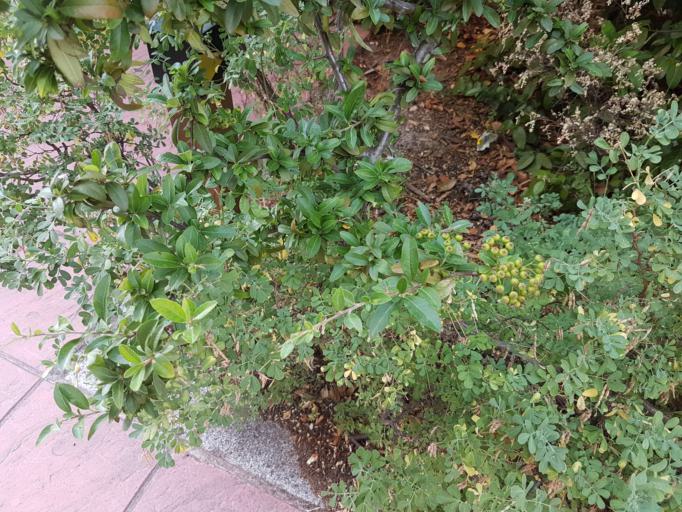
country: ES
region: Madrid
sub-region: Provincia de Madrid
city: Tetuan de las Victorias
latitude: 40.4502
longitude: -3.7222
